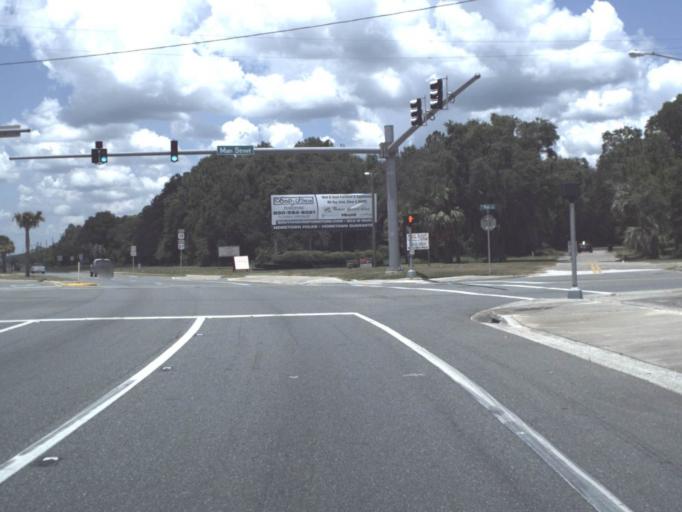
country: US
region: Florida
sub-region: Taylor County
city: Perry
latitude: 30.1176
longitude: -83.5892
